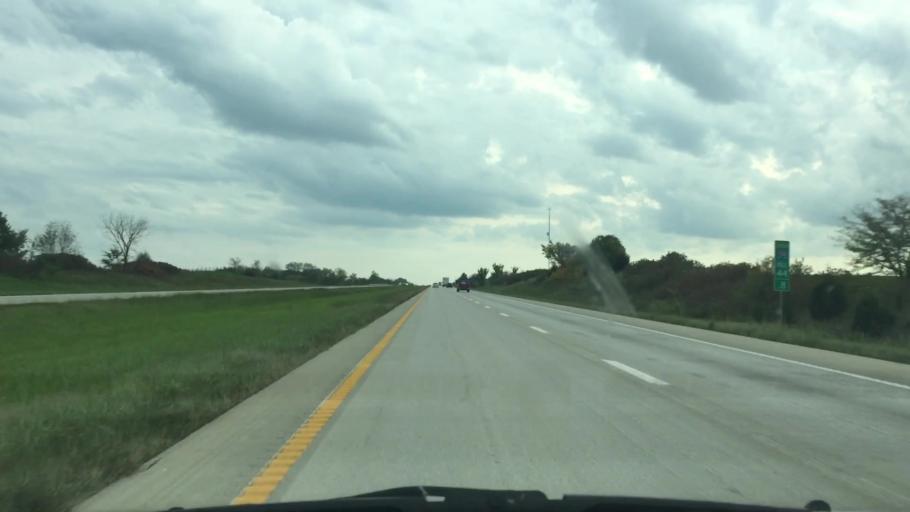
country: US
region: Missouri
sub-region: Clinton County
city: Lathrop
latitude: 39.6193
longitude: -94.2483
